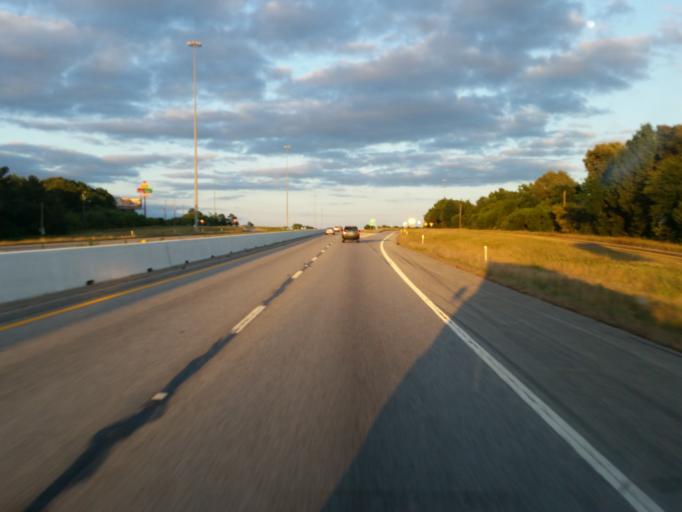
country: US
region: Texas
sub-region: Van Zandt County
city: Van
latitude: 32.5078
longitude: -95.6501
